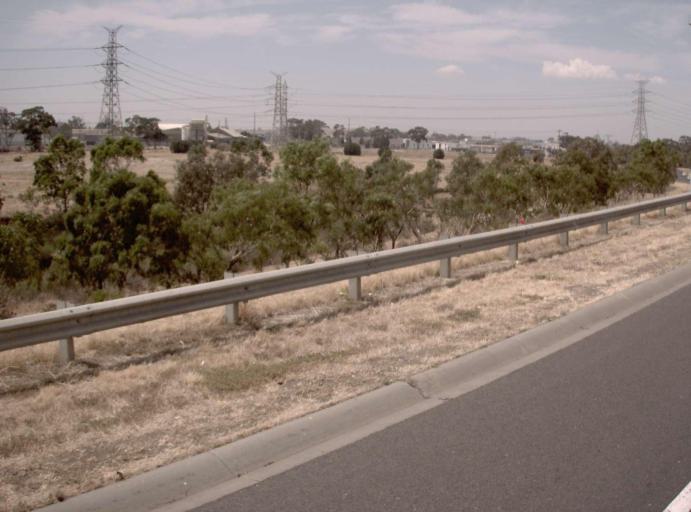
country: AU
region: Victoria
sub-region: Brimbank
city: Brooklyn
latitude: -37.8261
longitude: 144.8172
